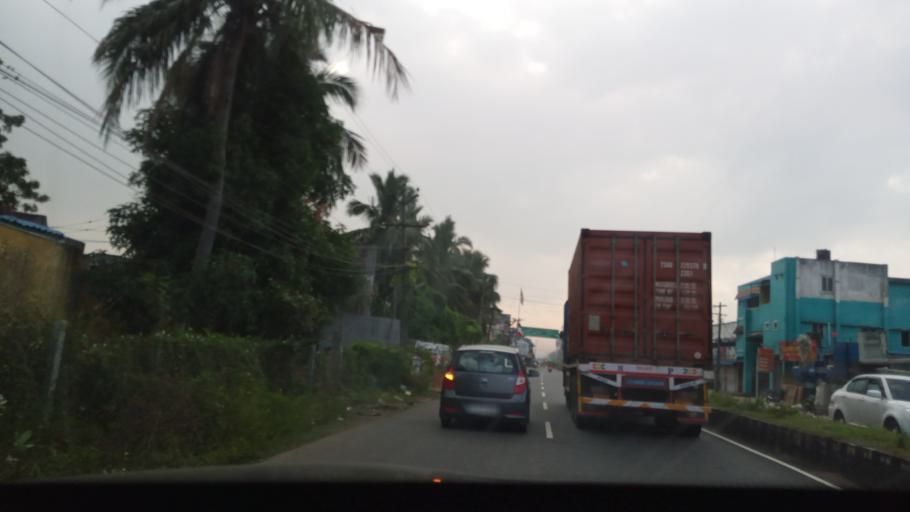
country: IN
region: Tamil Nadu
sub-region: Kancheepuram
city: Vengavasal
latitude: 12.8286
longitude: 80.1640
